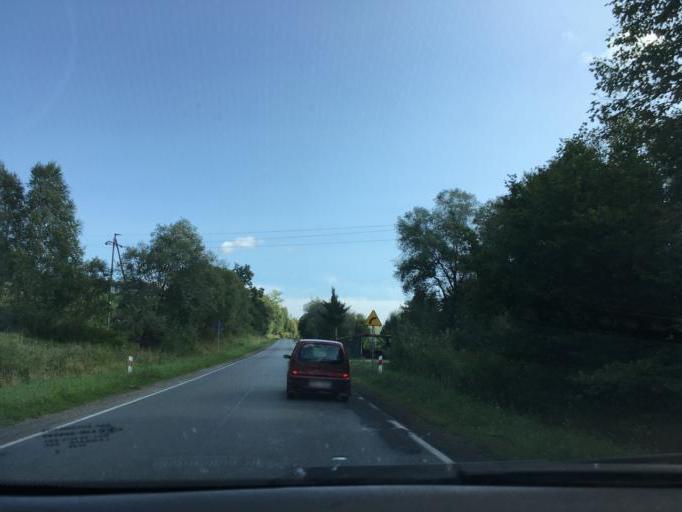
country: PL
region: Subcarpathian Voivodeship
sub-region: Powiat bieszczadzki
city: Ustrzyki Dolne
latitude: 49.3919
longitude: 22.6402
